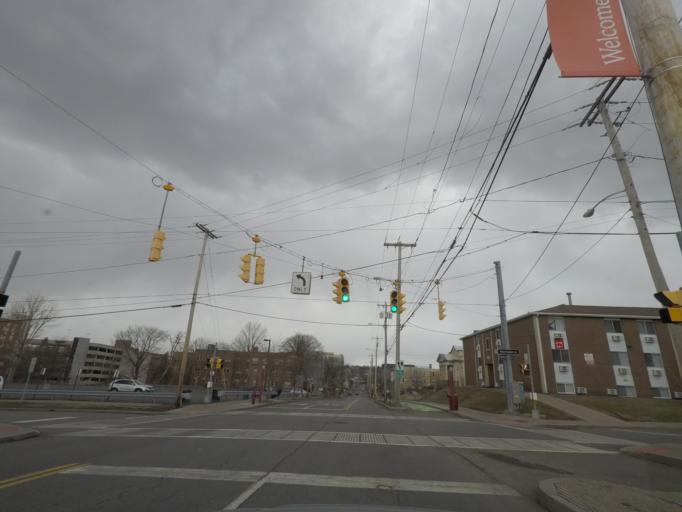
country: US
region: New York
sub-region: Onondaga County
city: Syracuse
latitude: 43.0441
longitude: -76.1344
